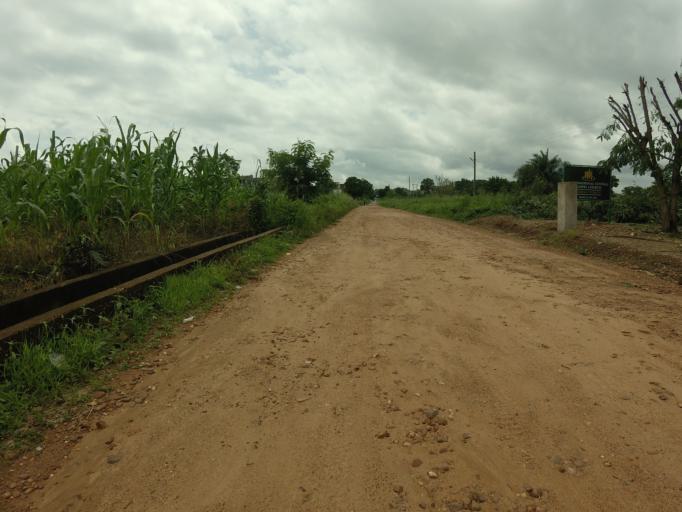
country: GH
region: Volta
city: Ho
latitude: 6.5879
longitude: 0.4607
